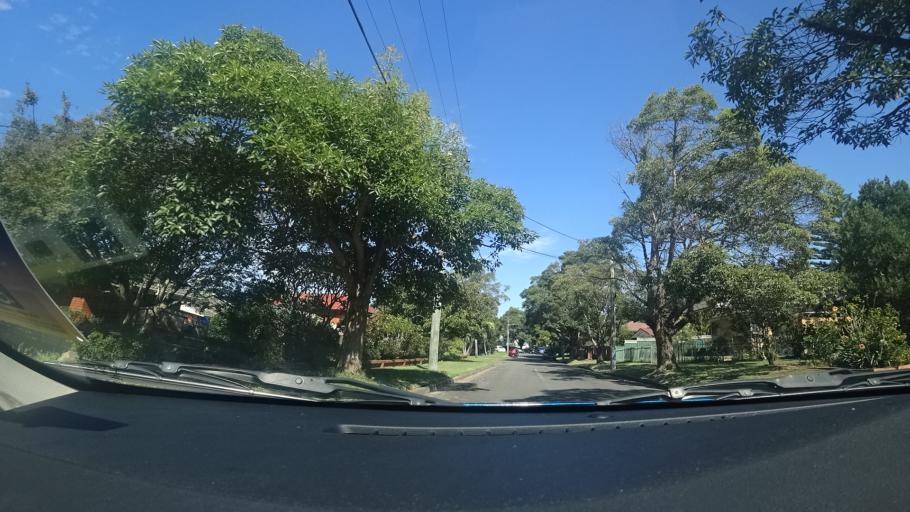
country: AU
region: New South Wales
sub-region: Warringah
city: Allambie Heights
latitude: -33.7597
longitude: 151.2485
